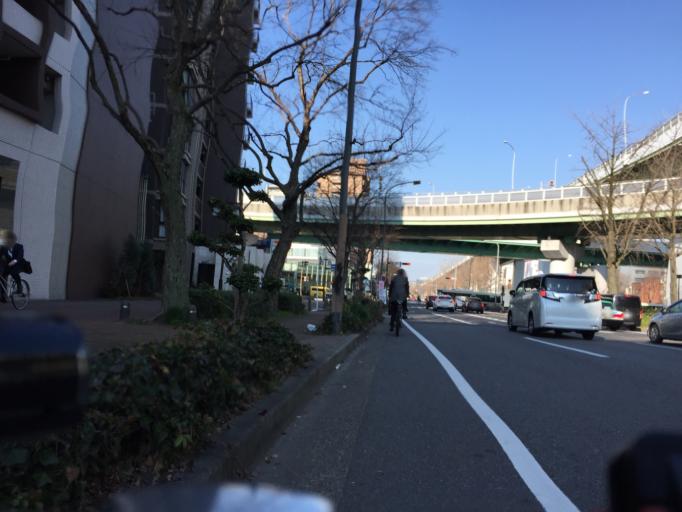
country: JP
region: Aichi
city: Nagoya-shi
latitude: 35.1608
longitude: 136.9169
